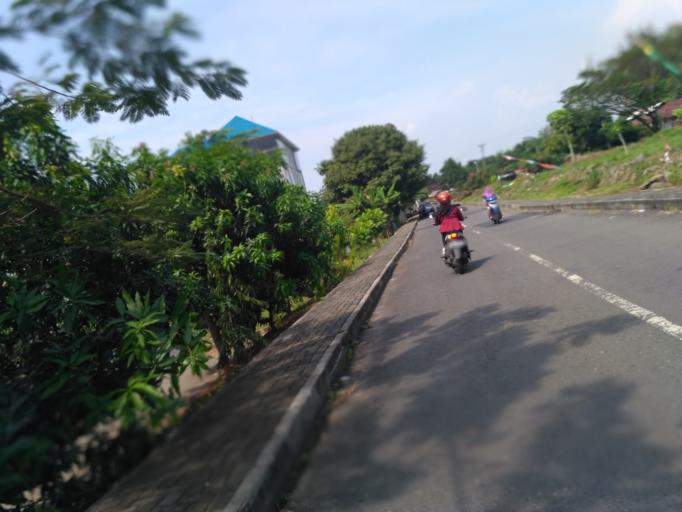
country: ID
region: Central Java
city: Semarang
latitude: -7.0518
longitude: 110.4418
